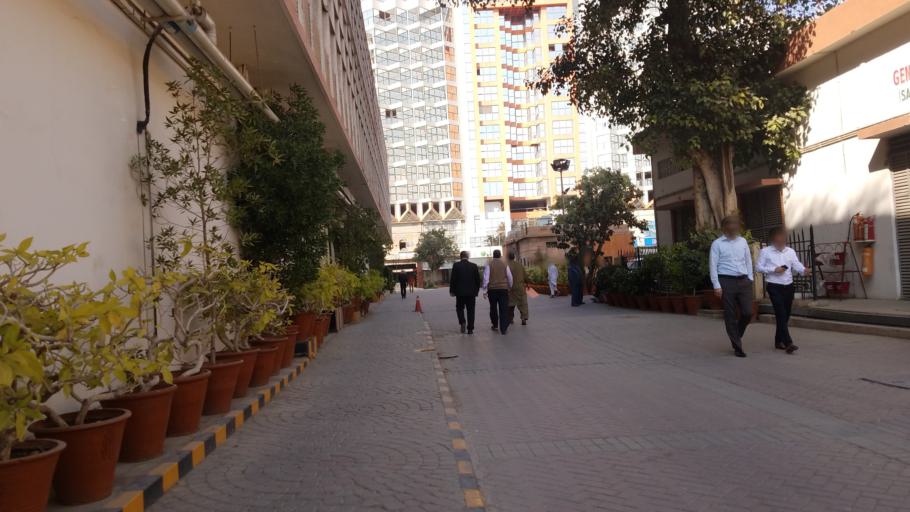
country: PK
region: Sindh
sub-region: Karachi District
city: Karachi
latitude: 24.8481
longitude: 66.9990
